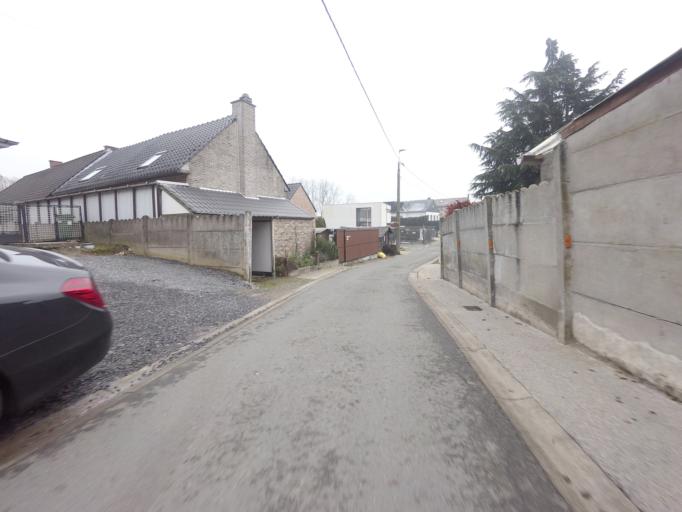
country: BE
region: Flanders
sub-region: Provincie Oost-Vlaanderen
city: Ninove
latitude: 50.8280
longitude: 3.9927
